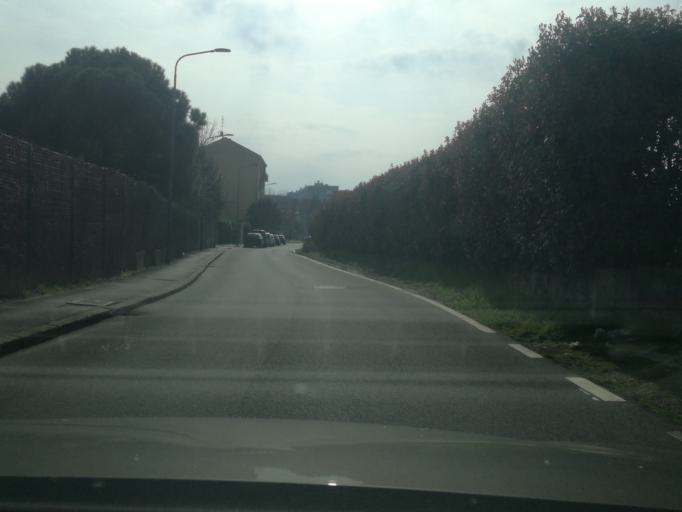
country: IT
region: Lombardy
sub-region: Citta metropolitana di Milano
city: Romano Banco
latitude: 45.4343
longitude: 9.1508
